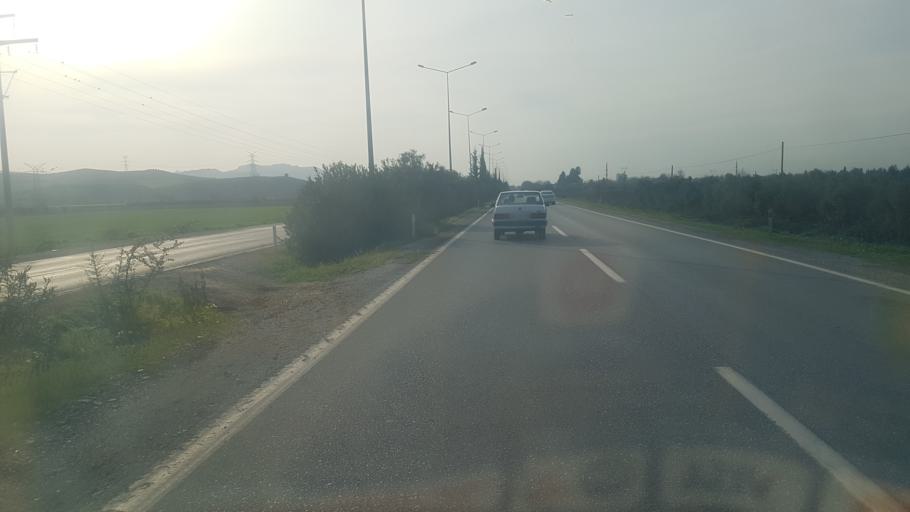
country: TR
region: Osmaniye
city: Toprakkale
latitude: 37.0544
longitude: 36.1369
